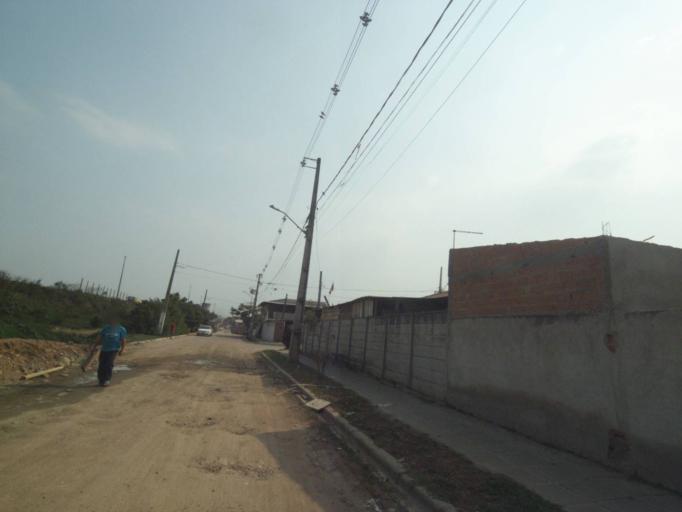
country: BR
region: Parana
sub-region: Sao Jose Dos Pinhais
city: Sao Jose dos Pinhais
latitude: -25.5302
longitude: -49.2307
